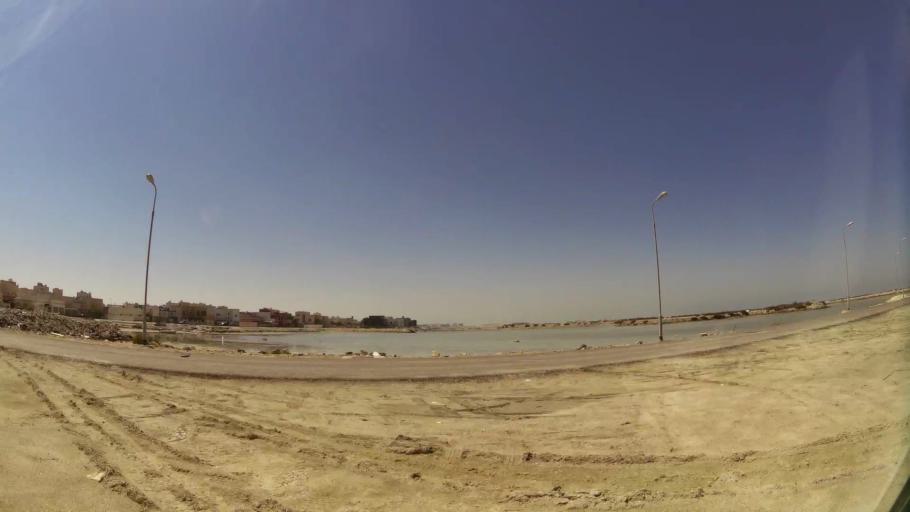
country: BH
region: Muharraq
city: Al Muharraq
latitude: 26.2896
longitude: 50.6246
